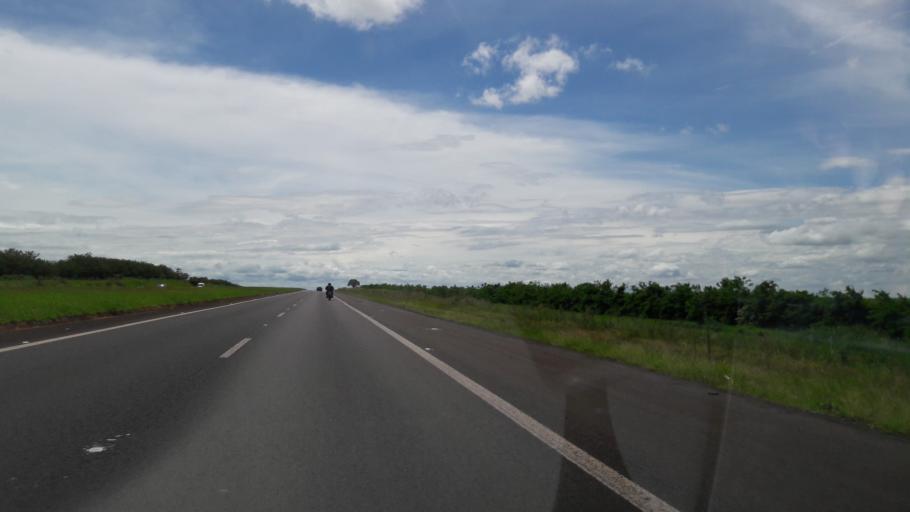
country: BR
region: Sao Paulo
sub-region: Avare
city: Avare
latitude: -22.9469
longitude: -48.8903
